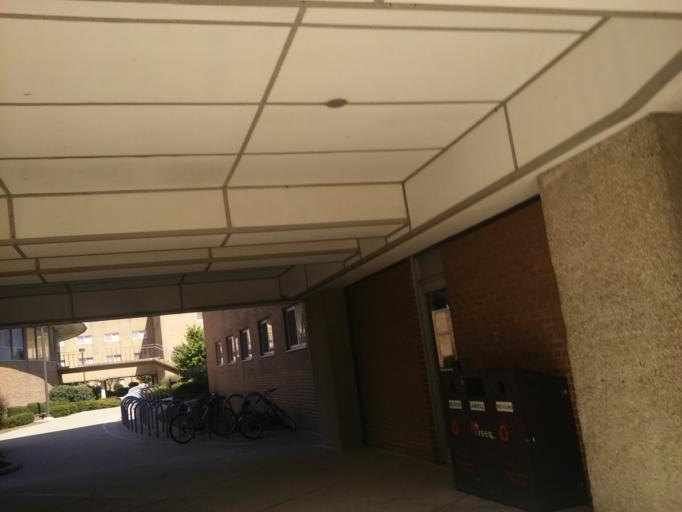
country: US
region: Ohio
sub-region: Wood County
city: Bowling Green
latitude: 41.3750
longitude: -83.6315
